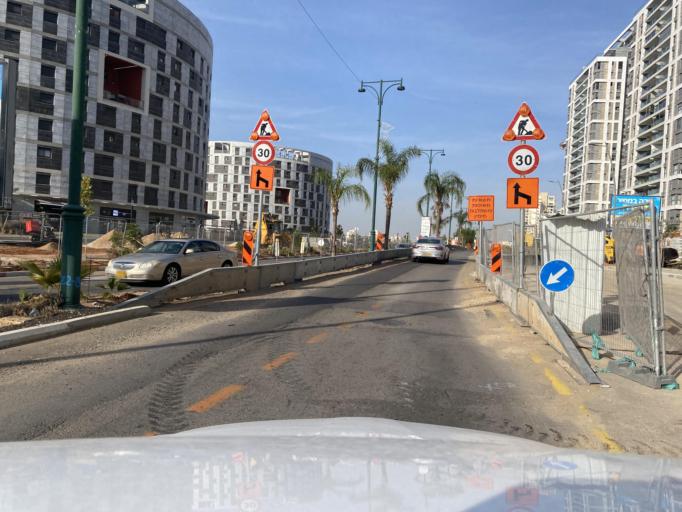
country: IL
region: Tel Aviv
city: Giv`at Shemu'el
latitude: 32.0704
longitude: 34.8505
